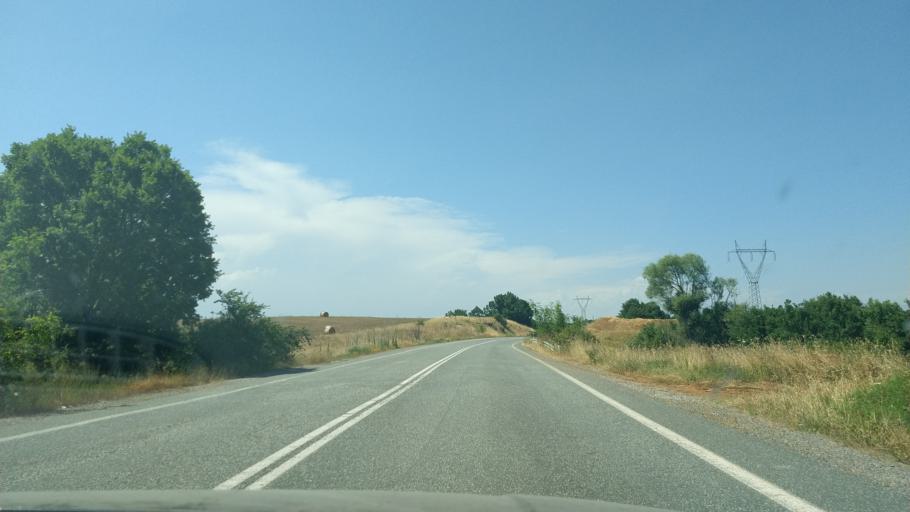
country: GR
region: West Macedonia
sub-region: Nomos Grevenon
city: Grevena
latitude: 40.0585
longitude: 21.4688
